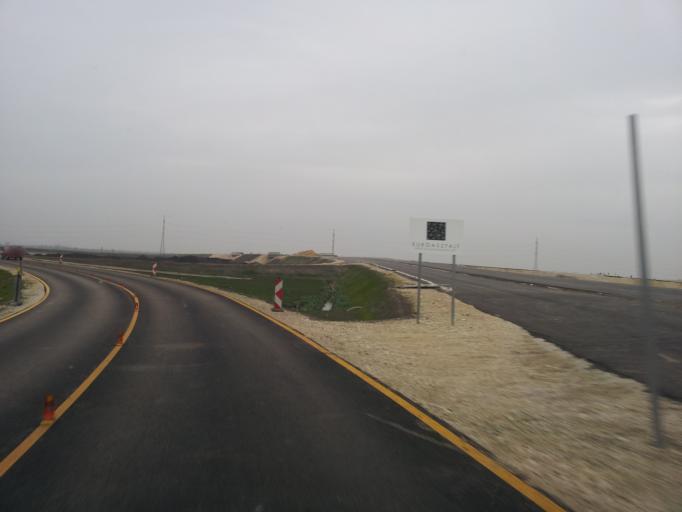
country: HU
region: Fejer
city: Szekesfehervar
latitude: 47.1794
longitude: 18.3800
